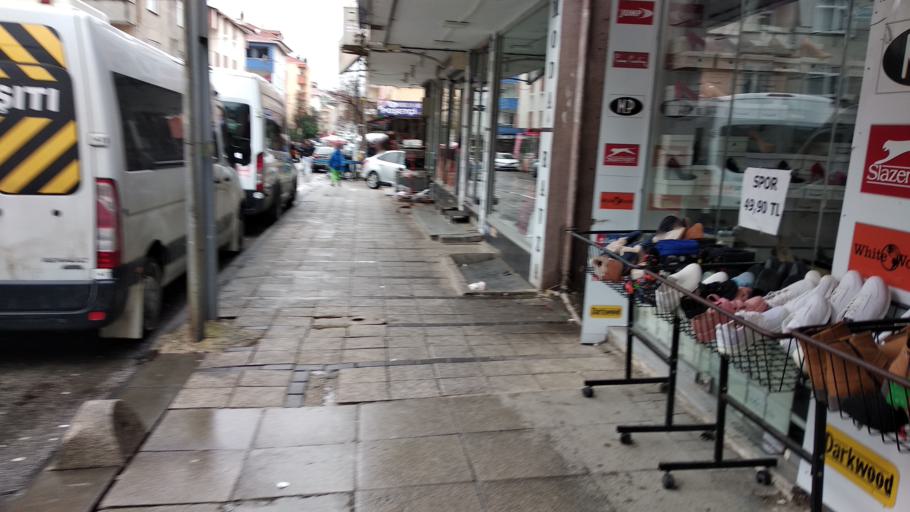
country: TR
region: Istanbul
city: Samandira
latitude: 41.0194
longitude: 29.1921
